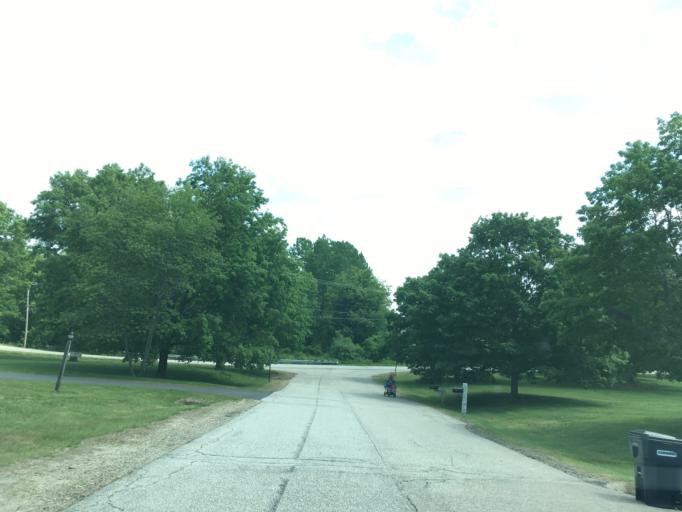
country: US
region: New Hampshire
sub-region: Rockingham County
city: Stratham Station
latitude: 43.0244
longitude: -70.8758
